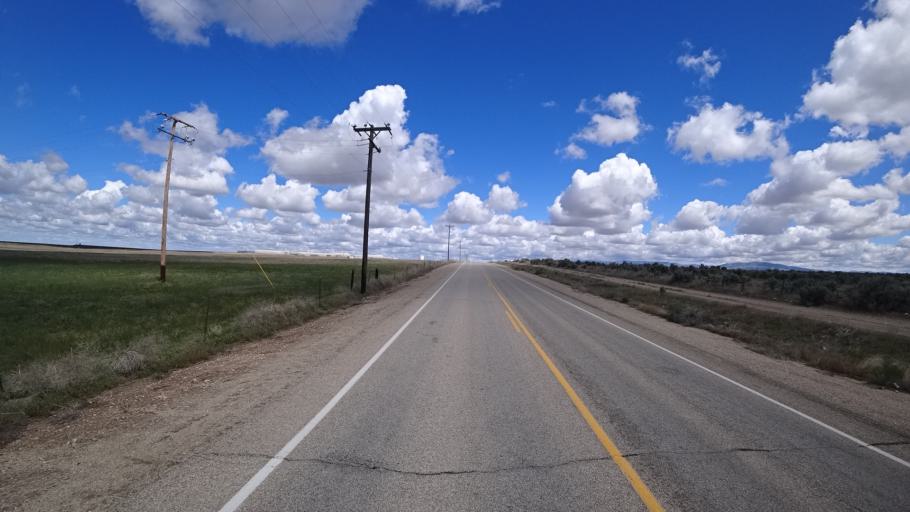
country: US
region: Idaho
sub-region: Ada County
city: Boise
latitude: 43.4646
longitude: -116.2344
